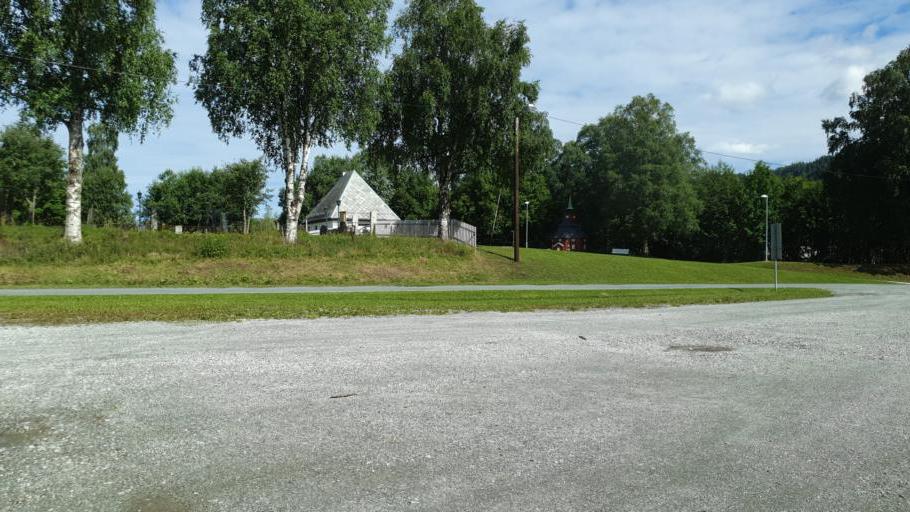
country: NO
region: Sor-Trondelag
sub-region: Midtre Gauldal
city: Storen
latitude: 63.0311
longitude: 10.2927
